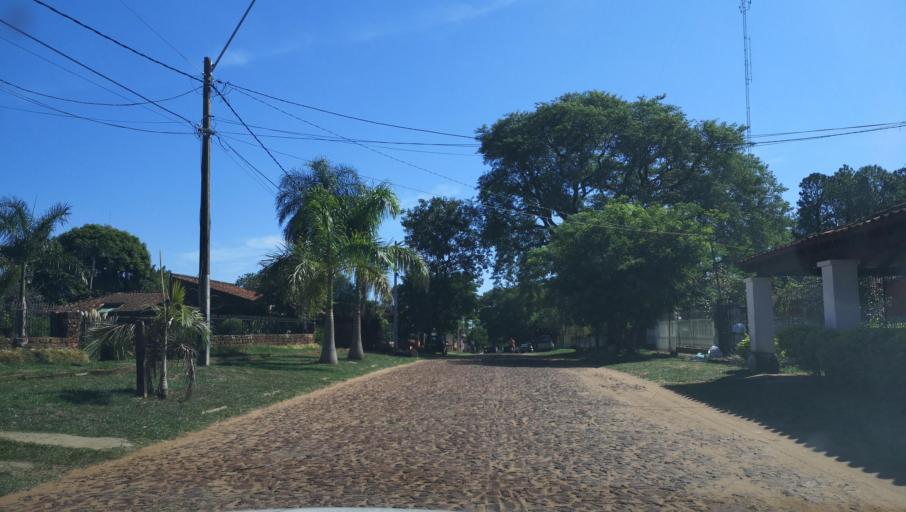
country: PY
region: Misiones
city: Santa Maria
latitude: -26.8909
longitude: -57.0250
